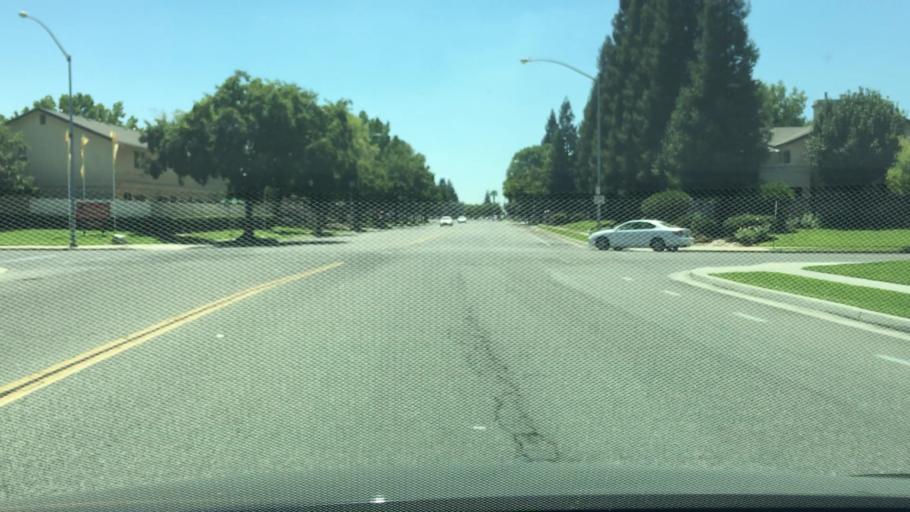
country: US
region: California
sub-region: Fresno County
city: Clovis
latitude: 36.8415
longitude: -119.7454
